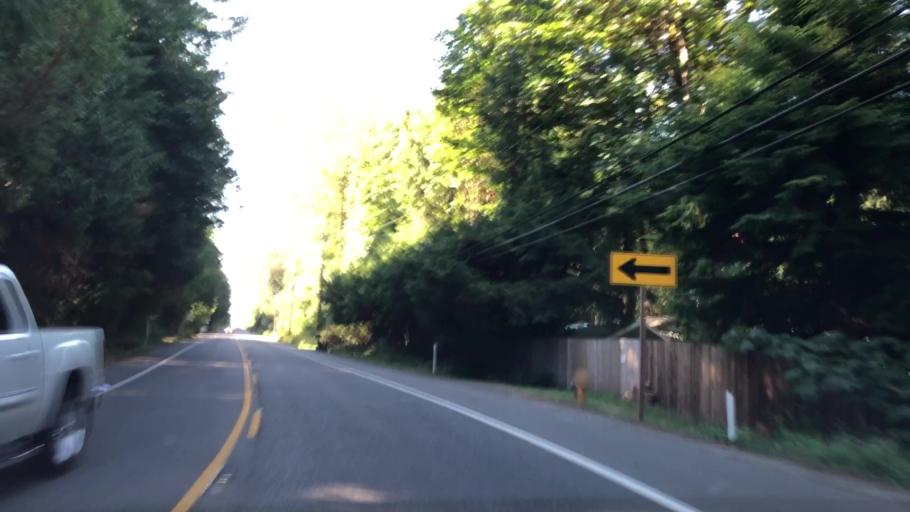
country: US
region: Washington
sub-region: Kitsap County
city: Kingston
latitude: 47.7921
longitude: -122.5058
